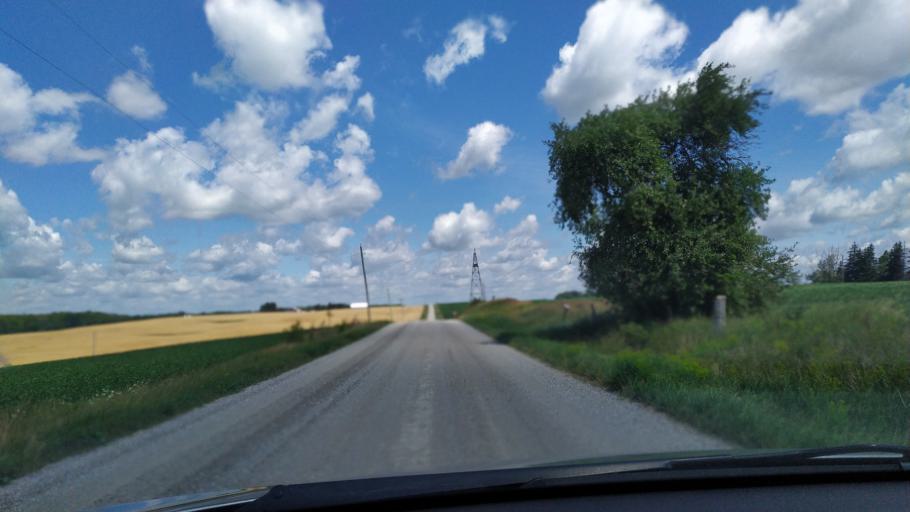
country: CA
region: Ontario
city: Stratford
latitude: 43.3858
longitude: -80.7619
